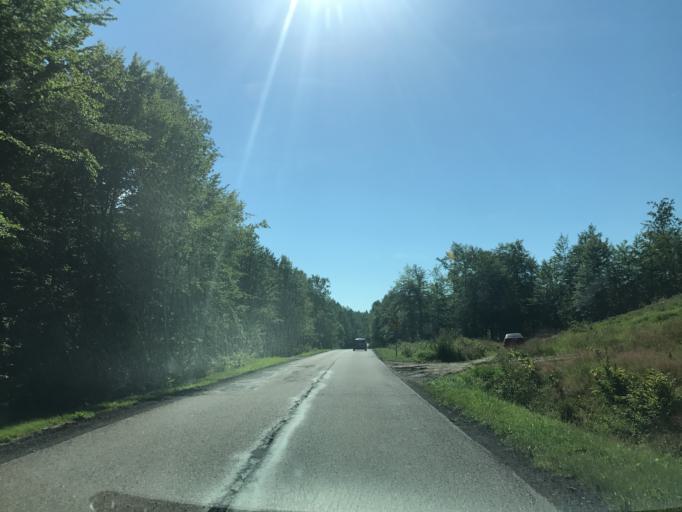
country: PL
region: Pomeranian Voivodeship
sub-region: Powiat slupski
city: Potegowo
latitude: 54.4090
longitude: 17.4400
